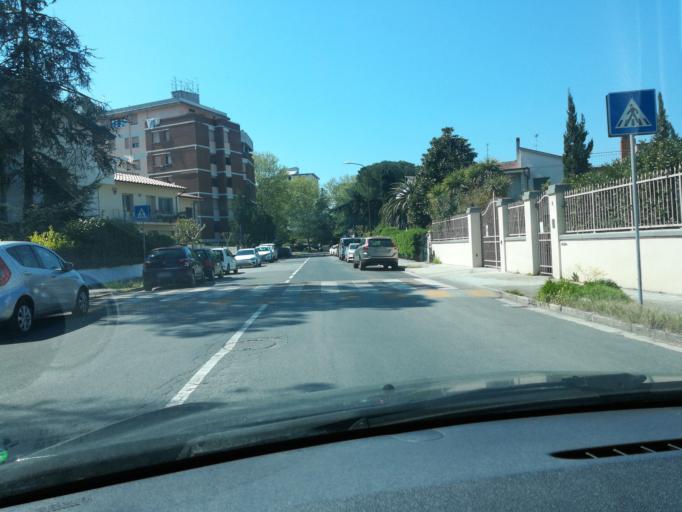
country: IT
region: Tuscany
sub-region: Province of Pisa
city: Pisa
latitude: 43.7333
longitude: 10.4043
